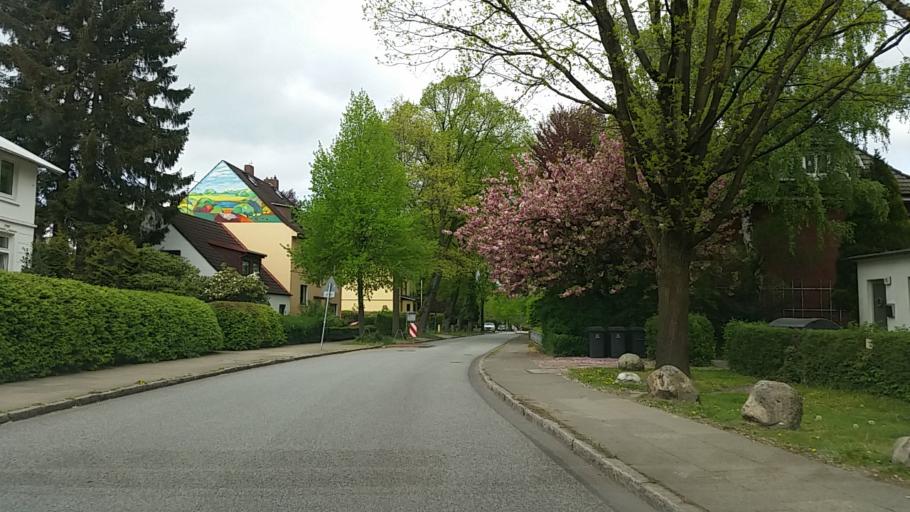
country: DE
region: Hamburg
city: Harburg
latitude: 53.4378
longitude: 10.0036
